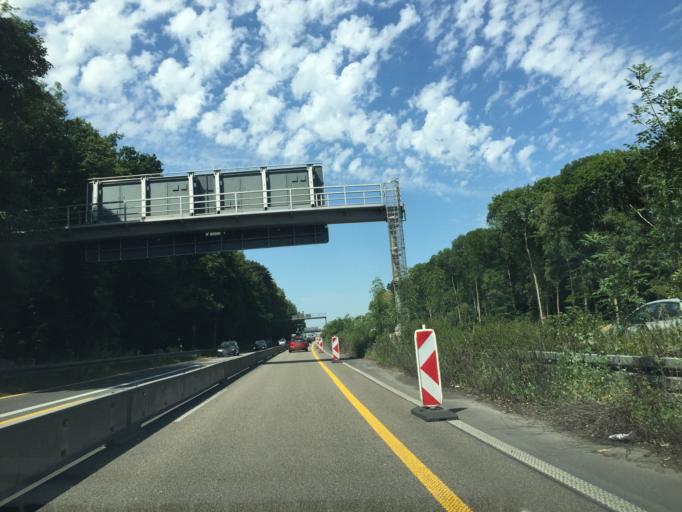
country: DE
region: North Rhine-Westphalia
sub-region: Regierungsbezirk Koln
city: Kerpen
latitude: 50.8901
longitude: 6.6683
